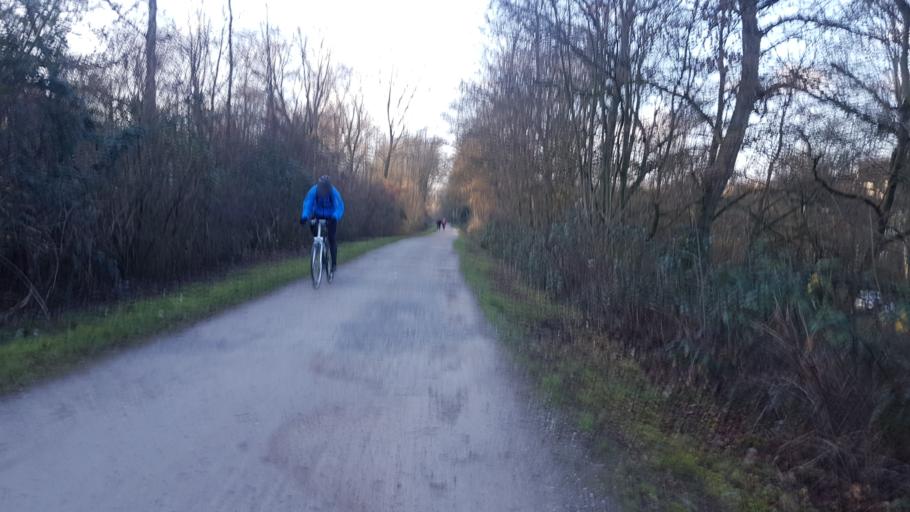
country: DE
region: North Rhine-Westphalia
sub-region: Regierungsbezirk Dusseldorf
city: Essen
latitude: 51.4355
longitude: 6.9785
